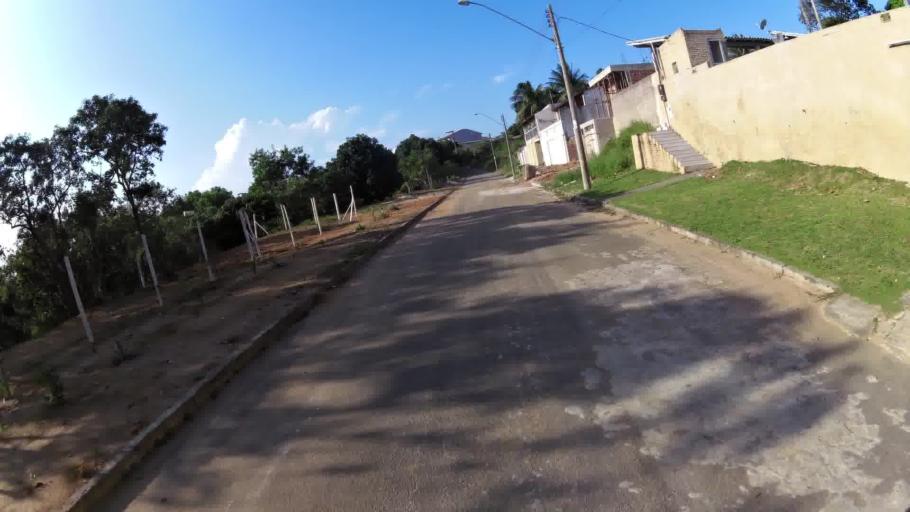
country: BR
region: Espirito Santo
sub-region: Guarapari
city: Guarapari
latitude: -20.7259
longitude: -40.5348
